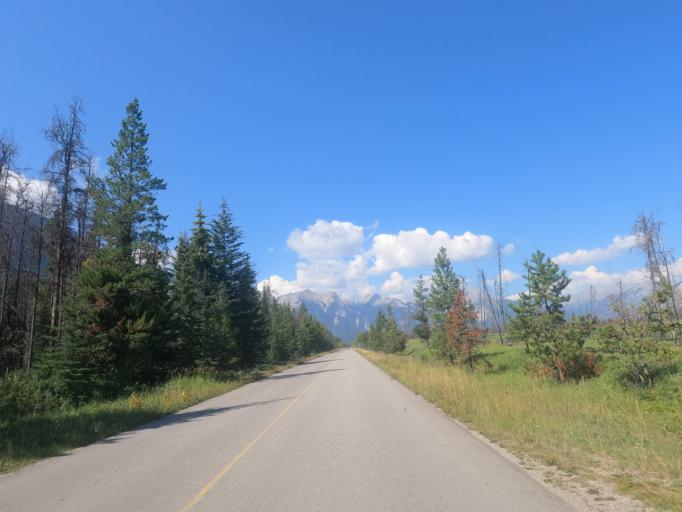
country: CA
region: Alberta
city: Jasper Park Lodge
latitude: 52.9765
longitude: -118.0660
